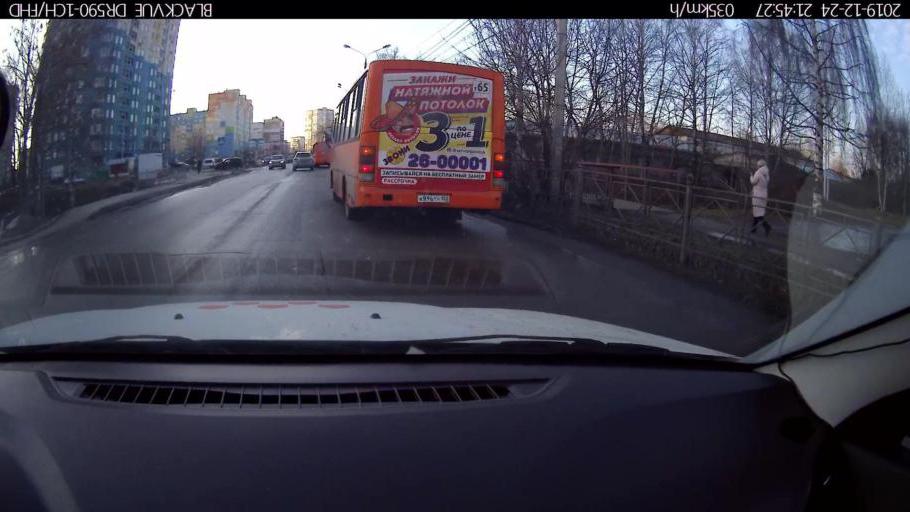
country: RU
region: Nizjnij Novgorod
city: Gorbatovka
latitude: 56.2402
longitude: 43.8422
